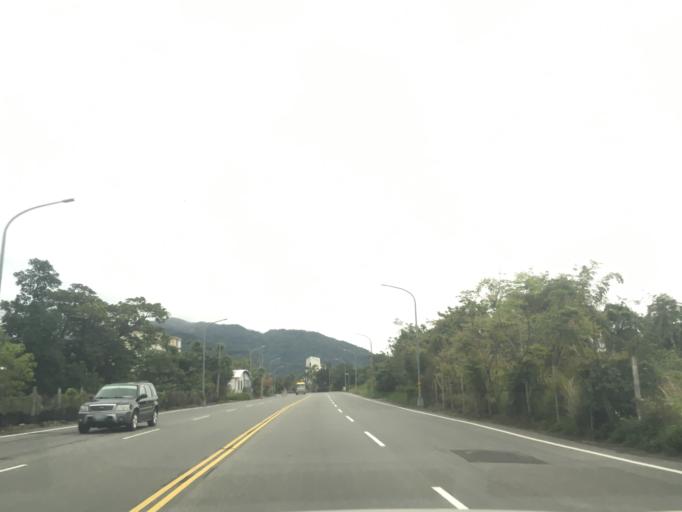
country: TW
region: Taiwan
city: Taitung City
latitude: 22.7446
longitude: 121.0570
